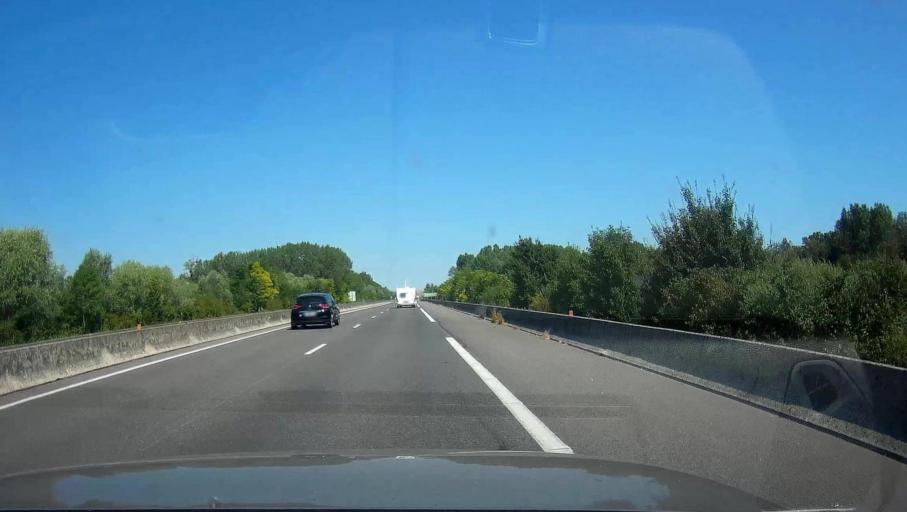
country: FR
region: Champagne-Ardenne
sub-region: Departement de l'Aube
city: Arcis-sur-Aube
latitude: 48.5359
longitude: 4.1844
